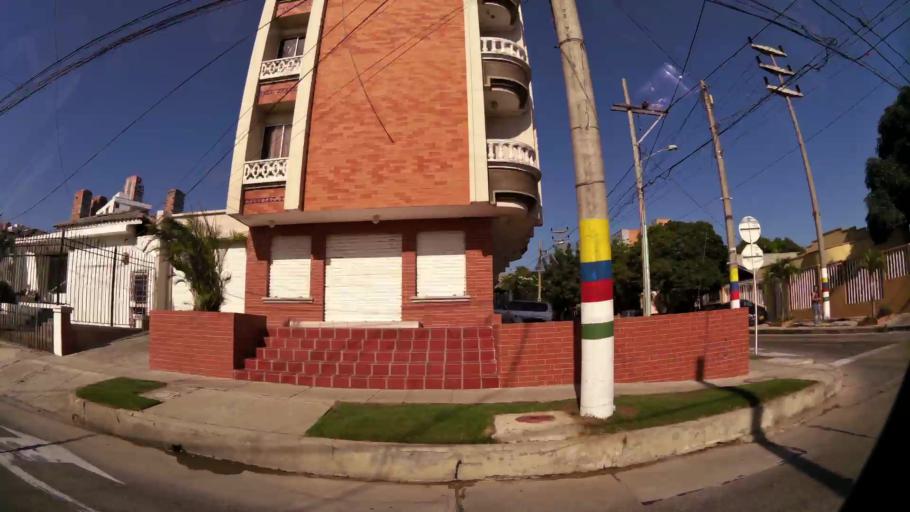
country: CO
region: Atlantico
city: Barranquilla
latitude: 11.0108
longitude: -74.8050
